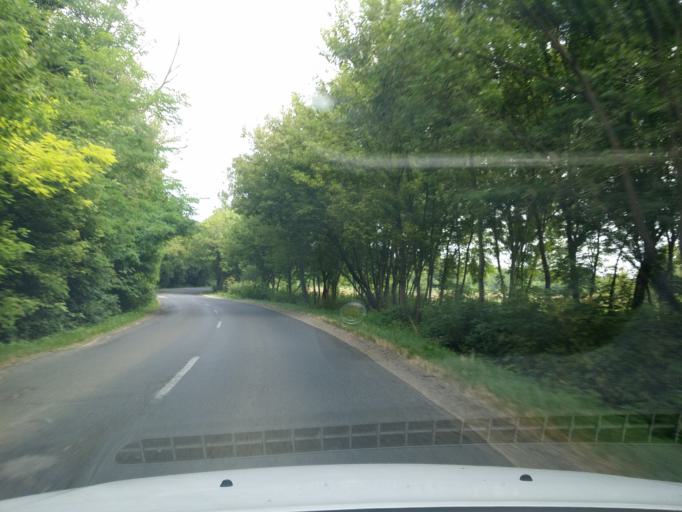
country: HU
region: Pest
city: Acsa
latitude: 47.8101
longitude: 19.3883
